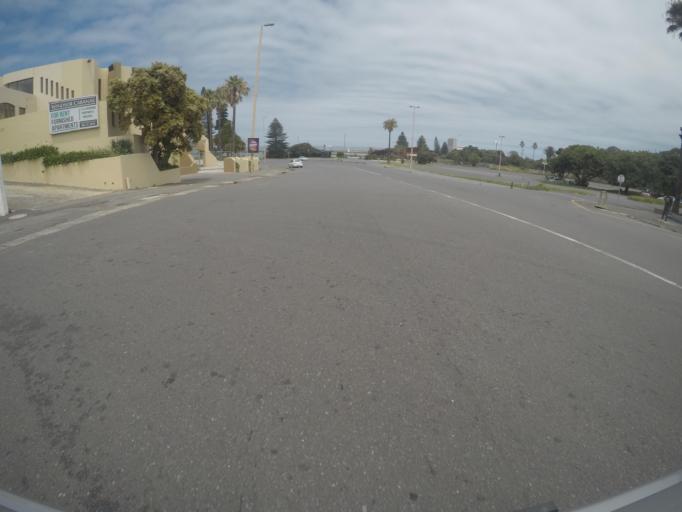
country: ZA
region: Eastern Cape
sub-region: Buffalo City Metropolitan Municipality
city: East London
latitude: -33.0216
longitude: 27.9146
